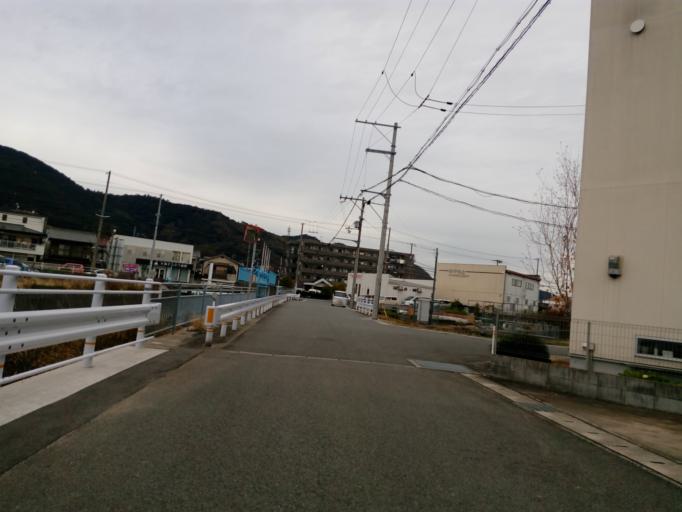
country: JP
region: Hyogo
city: Himeji
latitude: 34.8068
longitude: 134.6159
